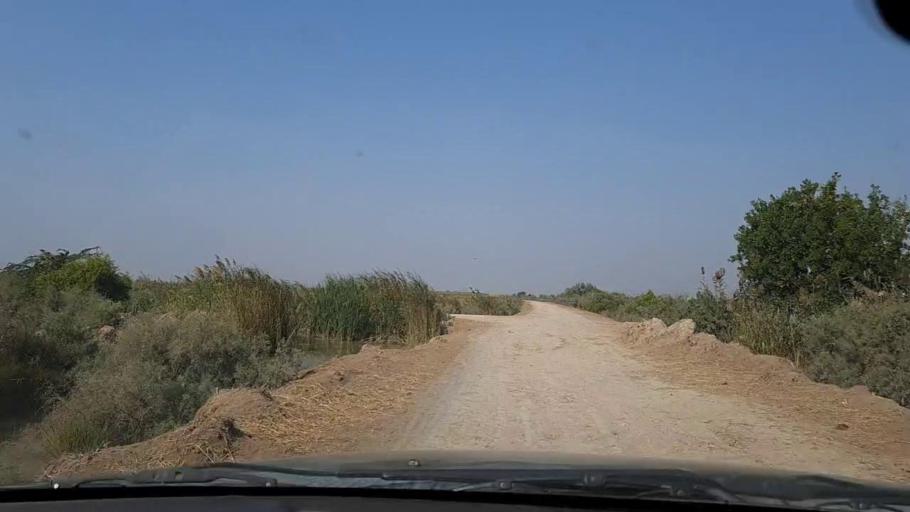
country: PK
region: Sindh
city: Mirpur Sakro
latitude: 24.3594
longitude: 67.6830
